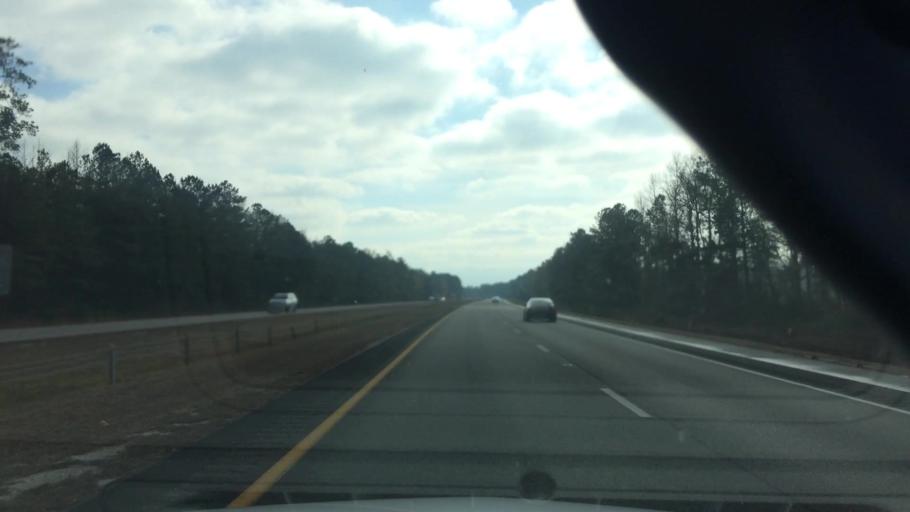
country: US
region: North Carolina
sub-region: Pender County
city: Burgaw
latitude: 34.5467
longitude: -77.8935
